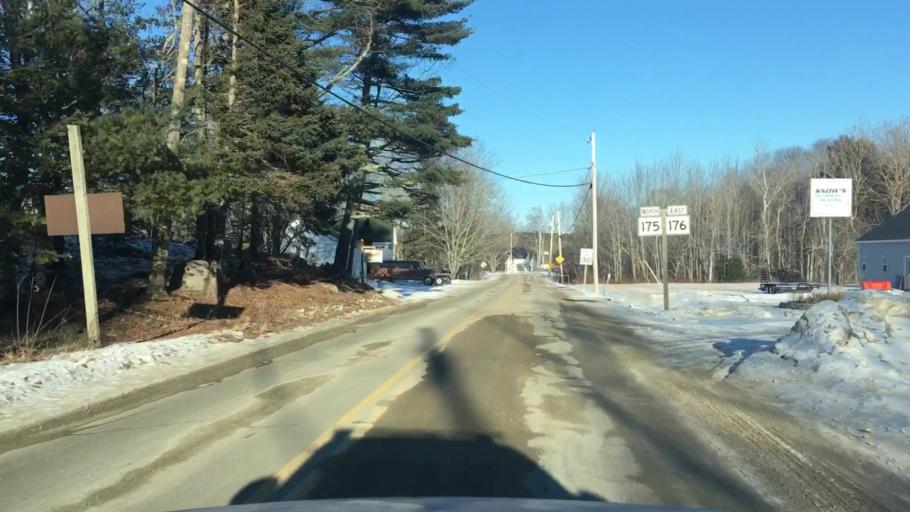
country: US
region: Maine
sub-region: Hancock County
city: Penobscot
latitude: 44.3957
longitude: -68.7099
